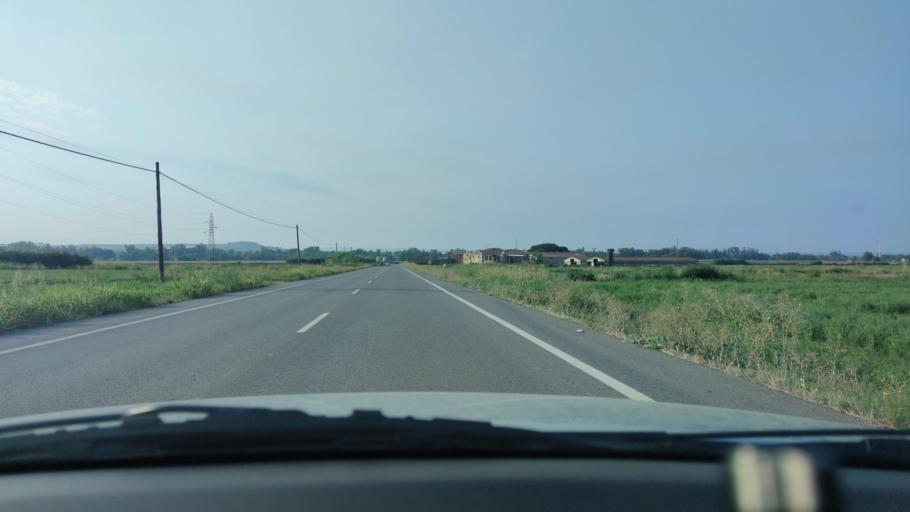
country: ES
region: Catalonia
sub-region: Provincia de Lleida
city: Torres de Segre
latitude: 41.5482
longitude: 0.5102
